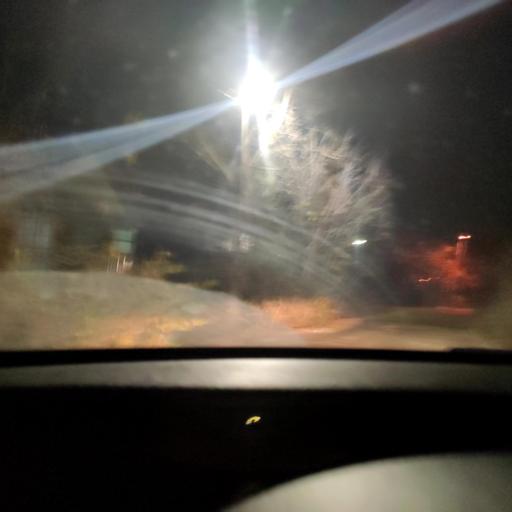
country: RU
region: Samara
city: Samara
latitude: 53.2167
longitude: 50.2151
